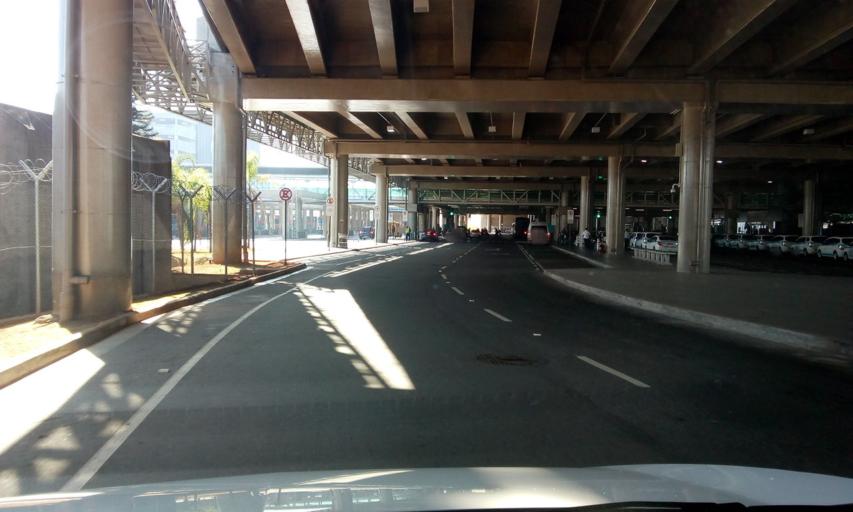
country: BR
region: Sao Paulo
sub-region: Guarulhos
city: Guarulhos
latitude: -23.4239
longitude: -46.4781
